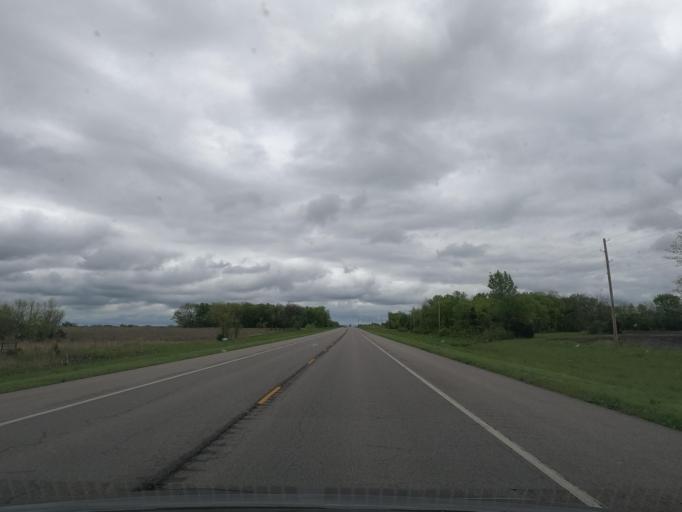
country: US
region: Kansas
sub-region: Labette County
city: Oswego
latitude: 37.3399
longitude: -95.0654
